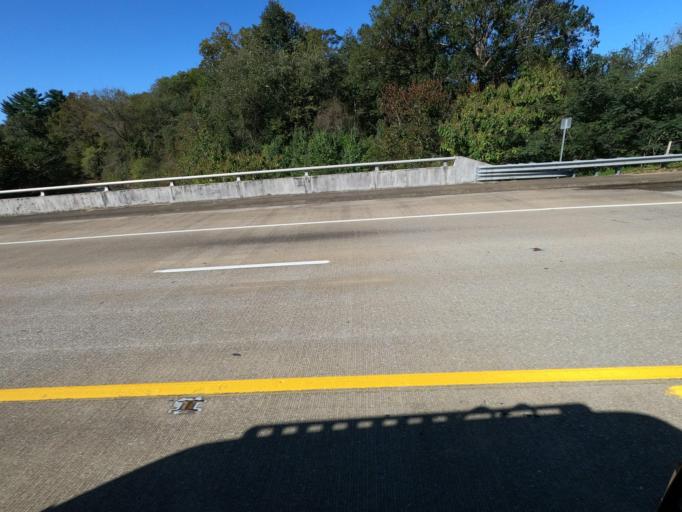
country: US
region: Tennessee
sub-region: Hamilton County
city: Sale Creek
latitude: 35.3863
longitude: -85.1080
